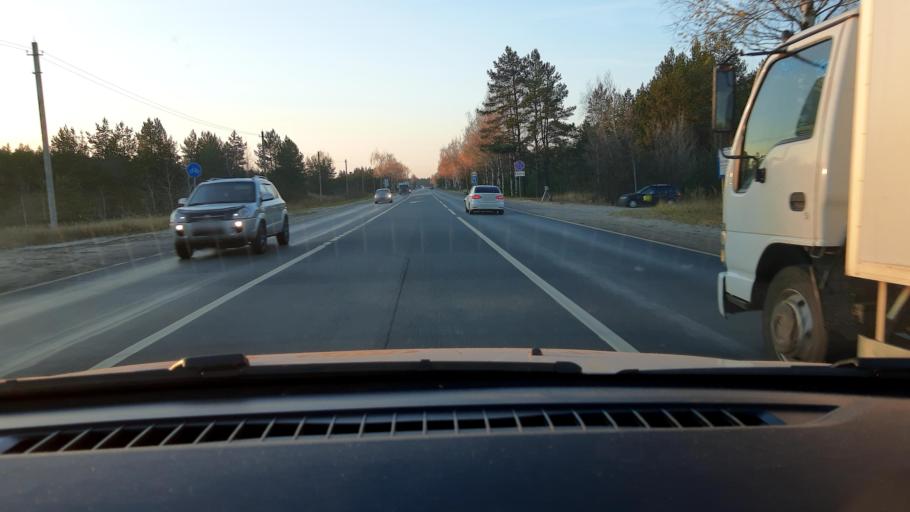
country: RU
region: Nizjnij Novgorod
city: Dzerzhinsk
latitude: 56.2844
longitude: 43.4755
